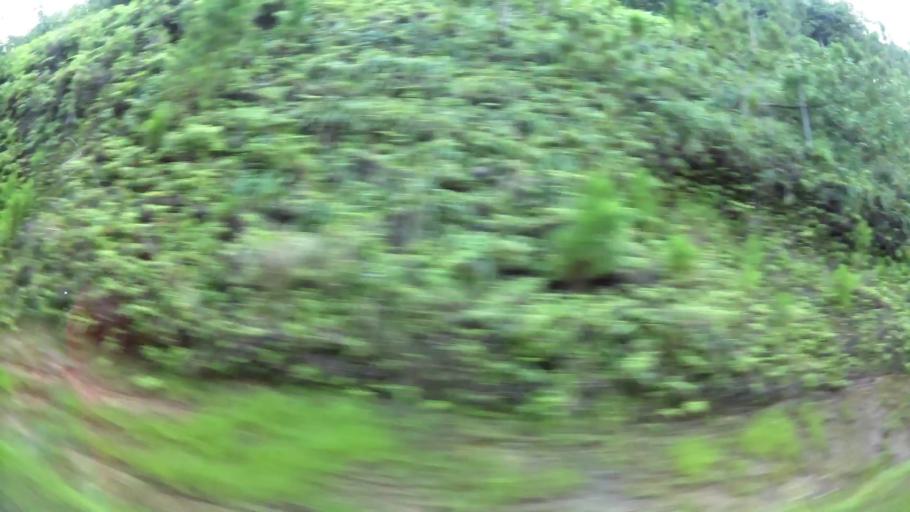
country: GP
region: Guadeloupe
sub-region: Guadeloupe
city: Bouillante
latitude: 16.1785
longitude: -61.7243
